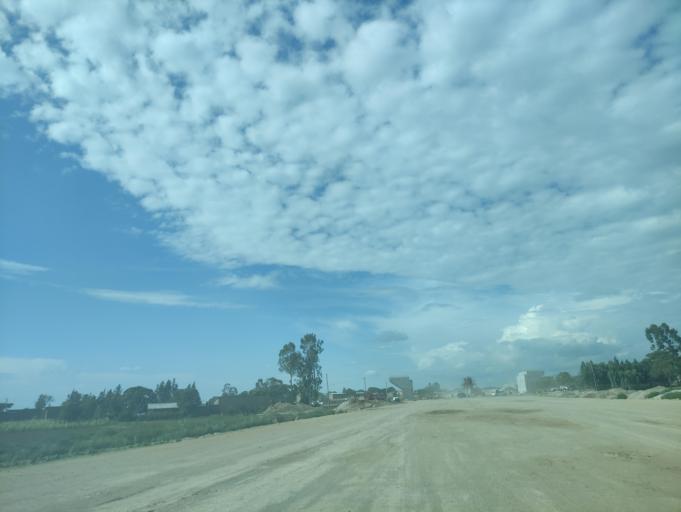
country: ET
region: Oromiya
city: Shashemene
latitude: 7.2217
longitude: 38.5584
